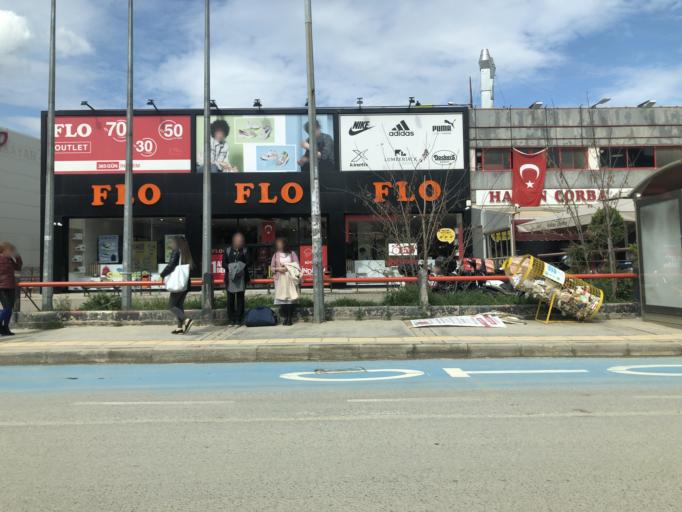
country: TR
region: Izmir
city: Karabaglar
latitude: 38.3949
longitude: 27.0561
